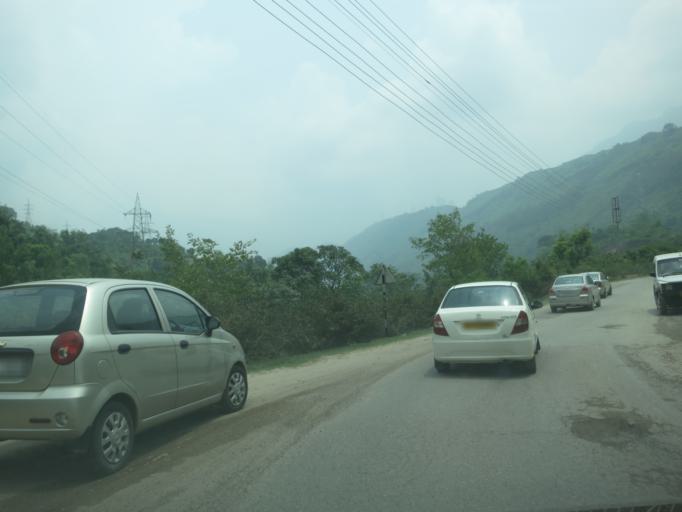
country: IN
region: Himachal Pradesh
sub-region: Mandi
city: Sundarnagar
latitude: 31.4516
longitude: 76.8548
